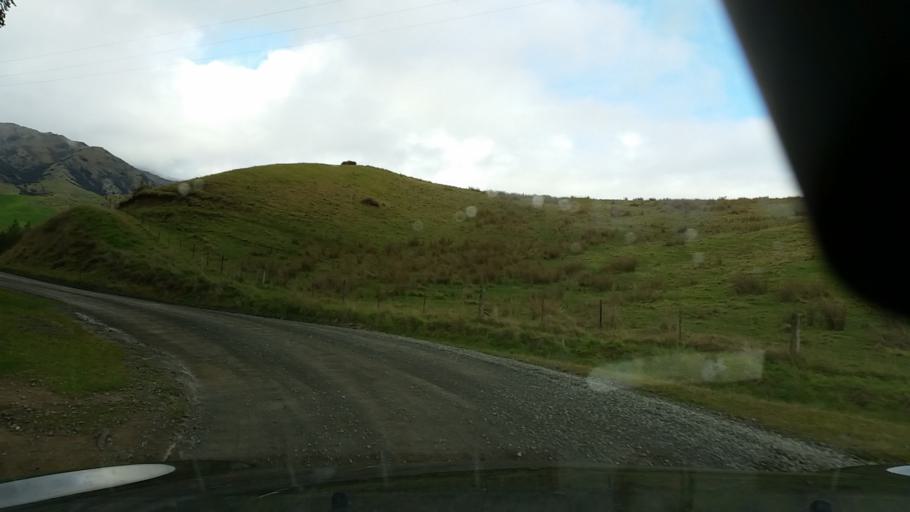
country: NZ
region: Marlborough
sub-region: Marlborough District
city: Blenheim
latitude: -41.6513
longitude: 173.6536
